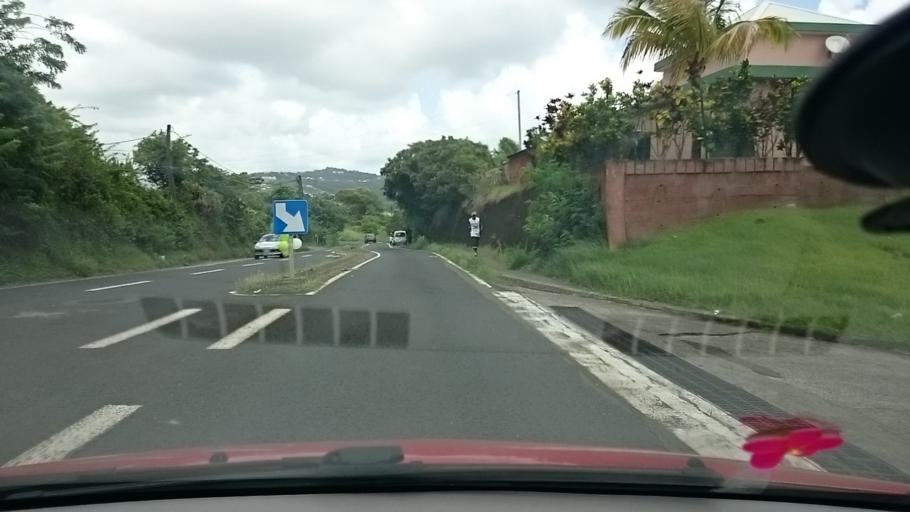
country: MQ
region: Martinique
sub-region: Martinique
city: La Trinite
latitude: 14.7388
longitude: -60.9499
